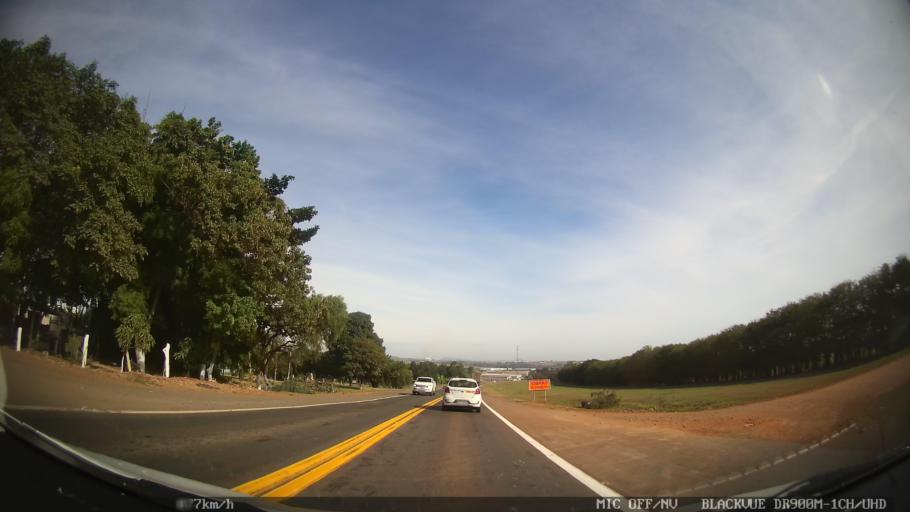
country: BR
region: Sao Paulo
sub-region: Rio Das Pedras
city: Rio das Pedras
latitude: -22.7970
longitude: -47.6078
